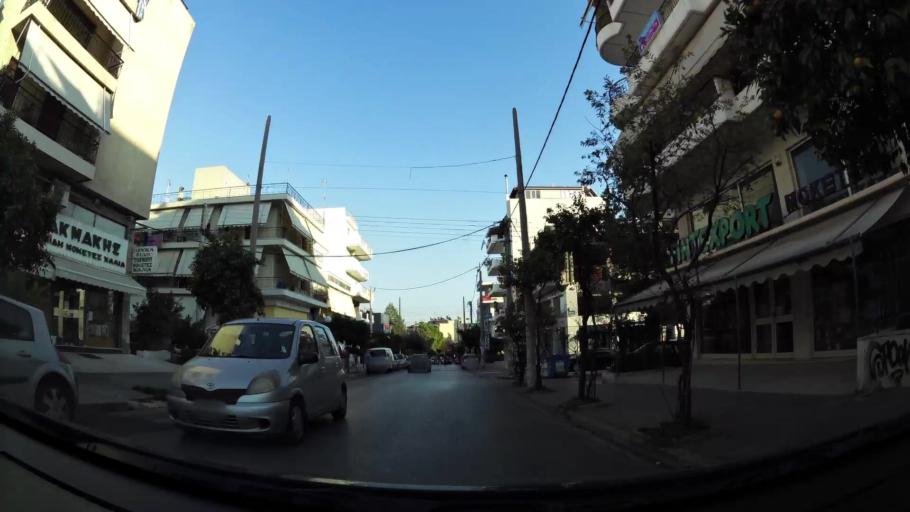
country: GR
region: Attica
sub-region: Nomos Piraios
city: Korydallos
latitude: 37.9764
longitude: 23.6398
